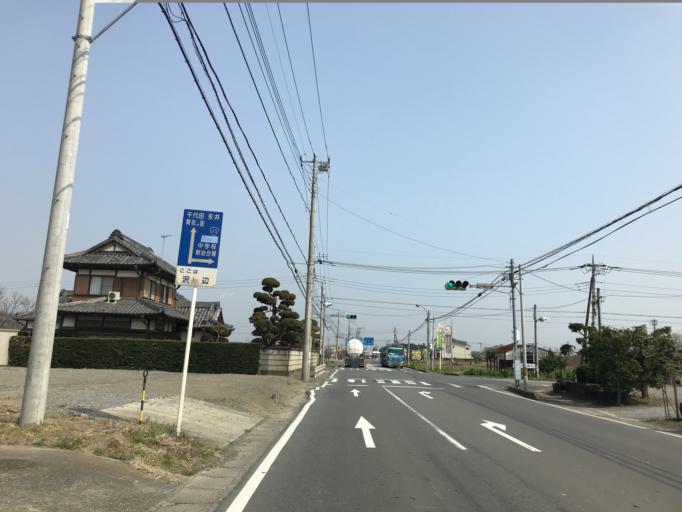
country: JP
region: Ibaraki
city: Tsukuba
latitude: 36.1482
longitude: 140.1615
